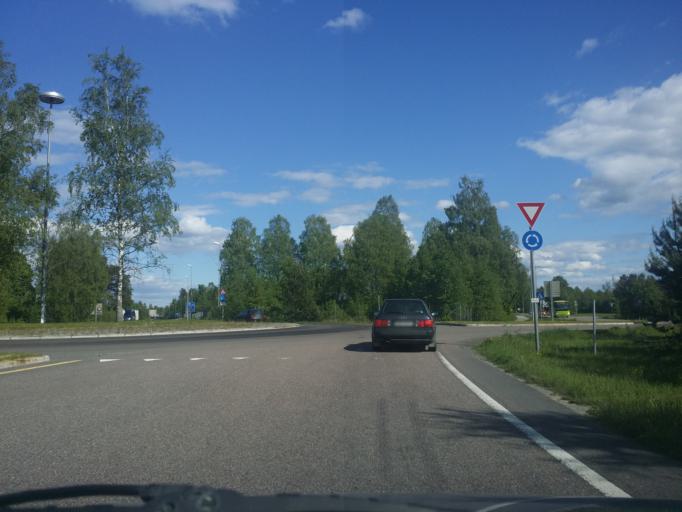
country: NO
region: Akershus
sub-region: Nannestad
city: Teigebyen
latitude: 60.1783
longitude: 11.0808
